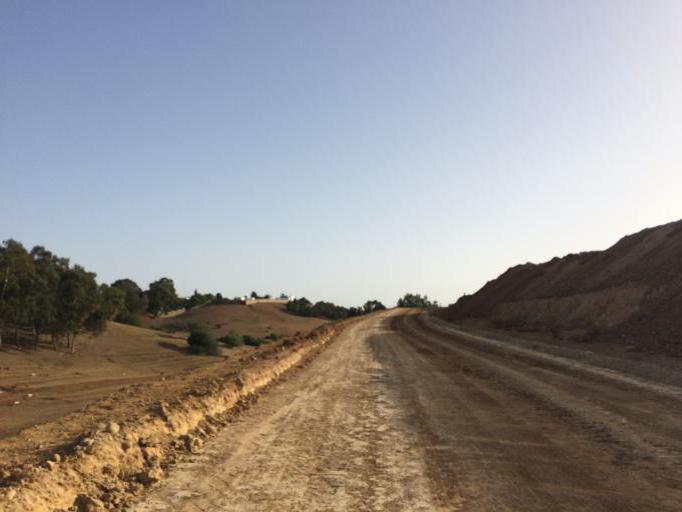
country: MA
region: Rabat-Sale-Zemmour-Zaer
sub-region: Rabat
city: Rabat
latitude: 34.0036
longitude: -6.8187
